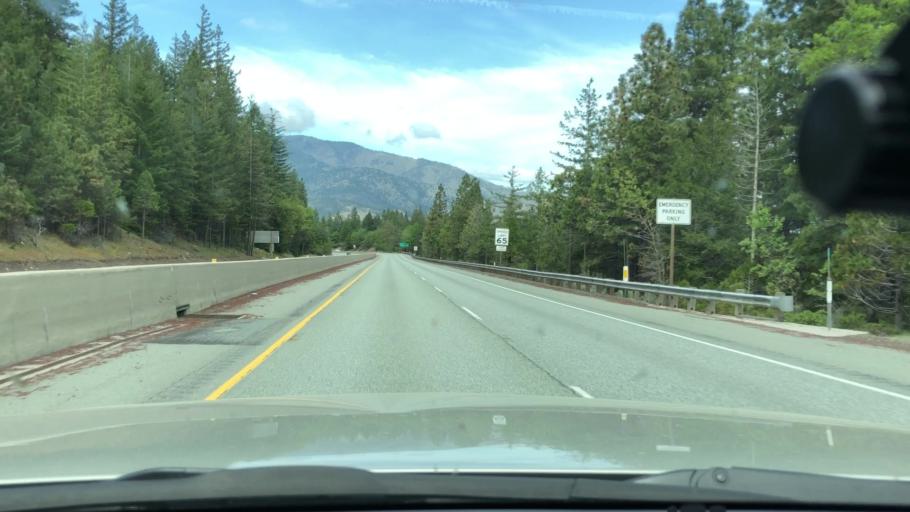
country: US
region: California
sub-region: Siskiyou County
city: Weed
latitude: 41.4298
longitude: -122.4037
